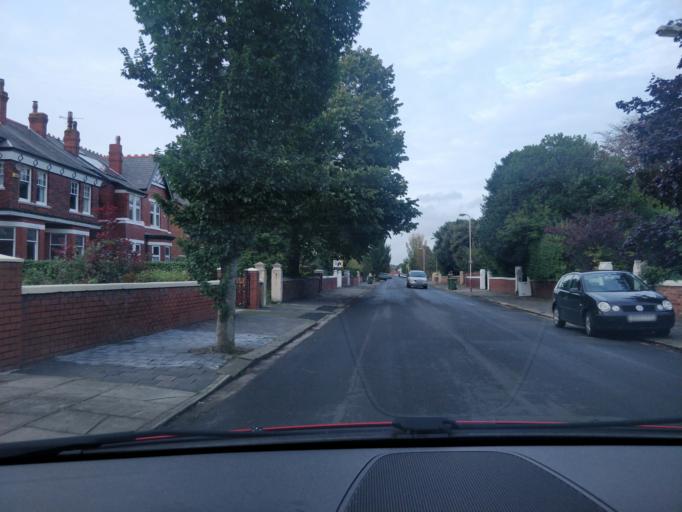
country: GB
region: England
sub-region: Sefton
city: Southport
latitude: 53.6391
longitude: -2.9890
